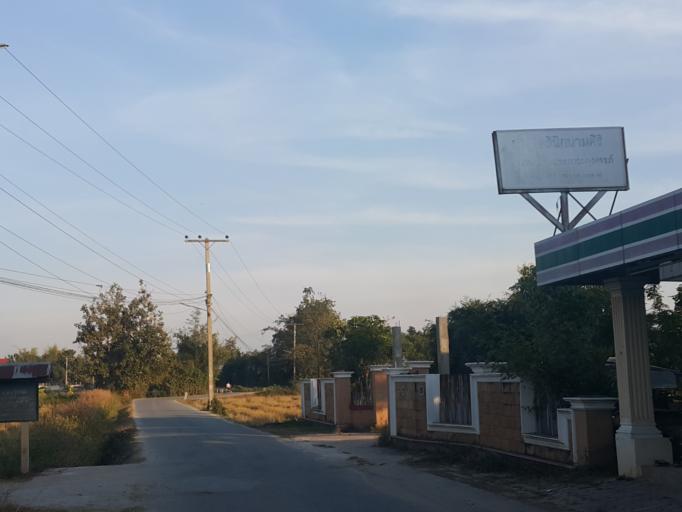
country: TH
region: Chiang Mai
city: San Sai
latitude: 18.8209
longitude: 99.0942
